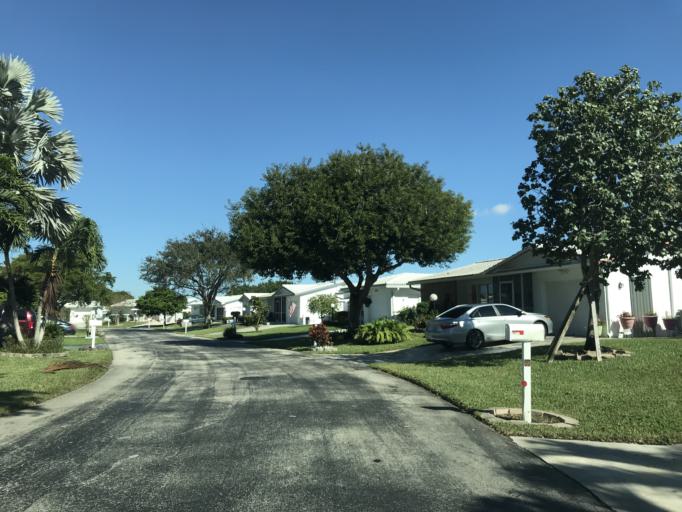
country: US
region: Florida
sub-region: Broward County
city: Plantation
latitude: 26.1373
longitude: -80.2675
